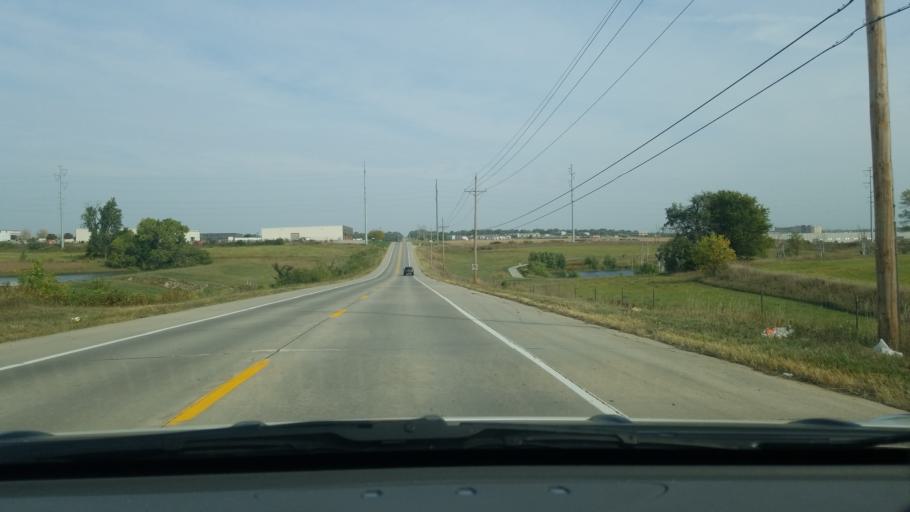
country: US
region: Nebraska
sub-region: Sarpy County
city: Chalco
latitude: 41.1655
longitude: -96.1196
